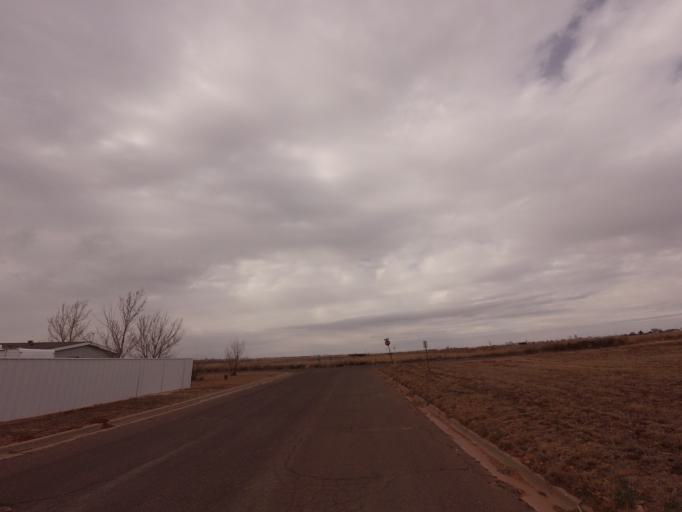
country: US
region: New Mexico
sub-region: Curry County
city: Clovis
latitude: 34.3824
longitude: -103.2048
